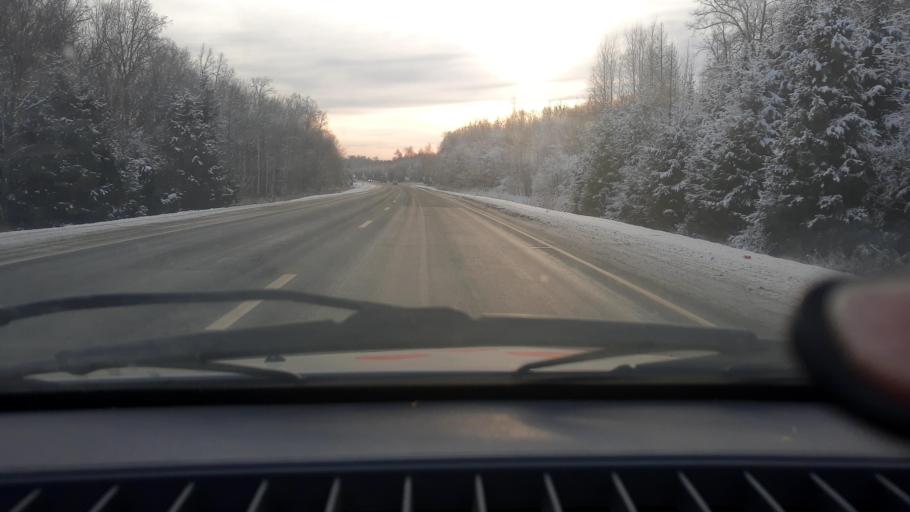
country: RU
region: Bashkortostan
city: Avdon
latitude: 54.8028
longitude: 55.7470
